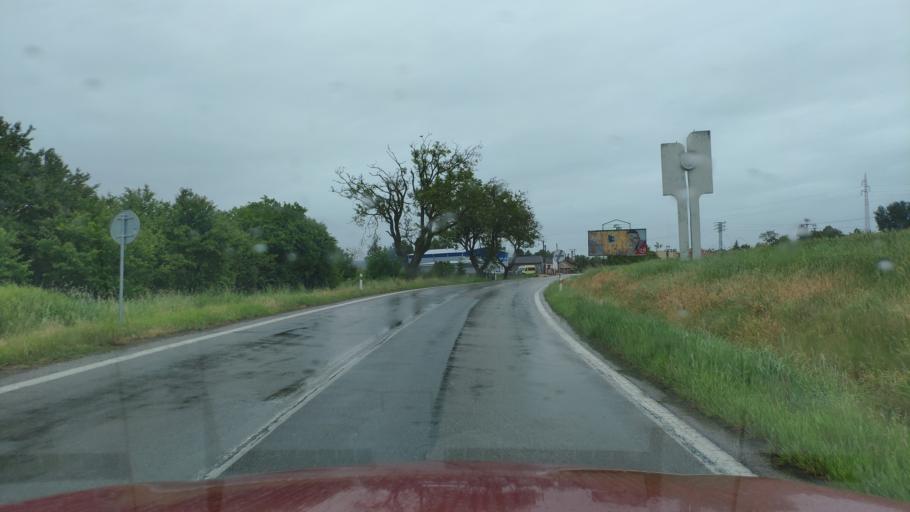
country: HU
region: Borsod-Abauj-Zemplen
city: Ricse
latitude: 48.4339
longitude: 21.9642
